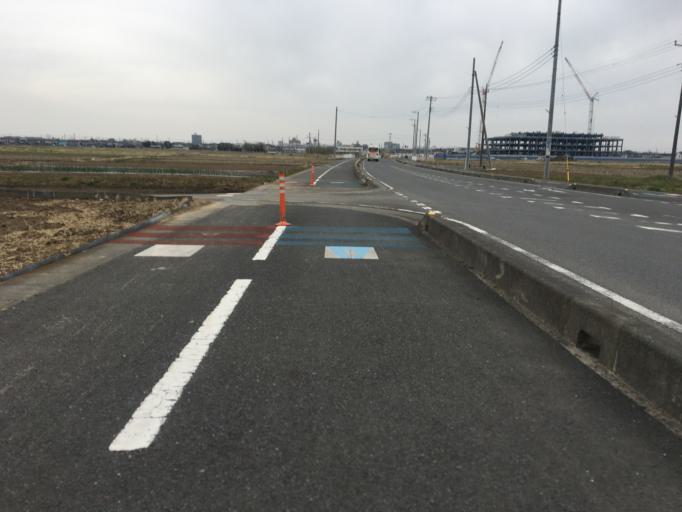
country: JP
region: Saitama
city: Kazo
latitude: 36.1148
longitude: 139.5899
